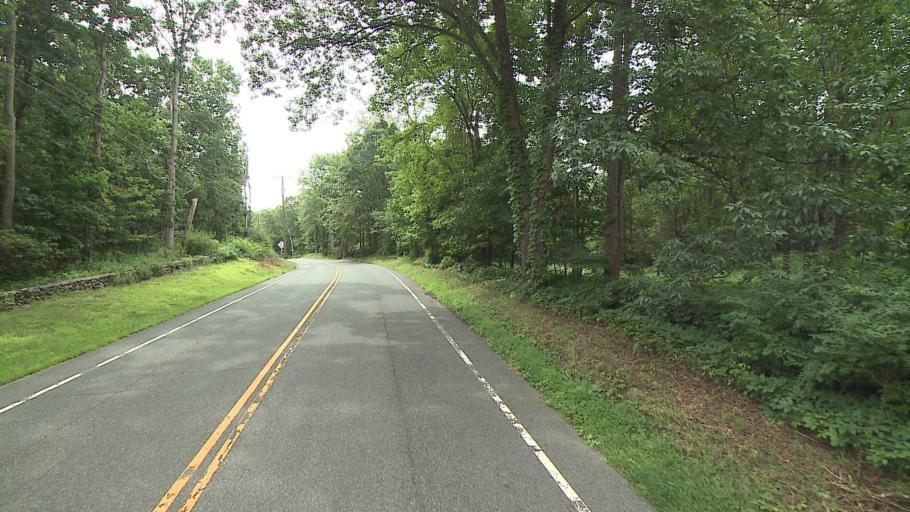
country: US
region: Connecticut
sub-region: Litchfield County
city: New Preston
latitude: 41.6141
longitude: -73.2912
